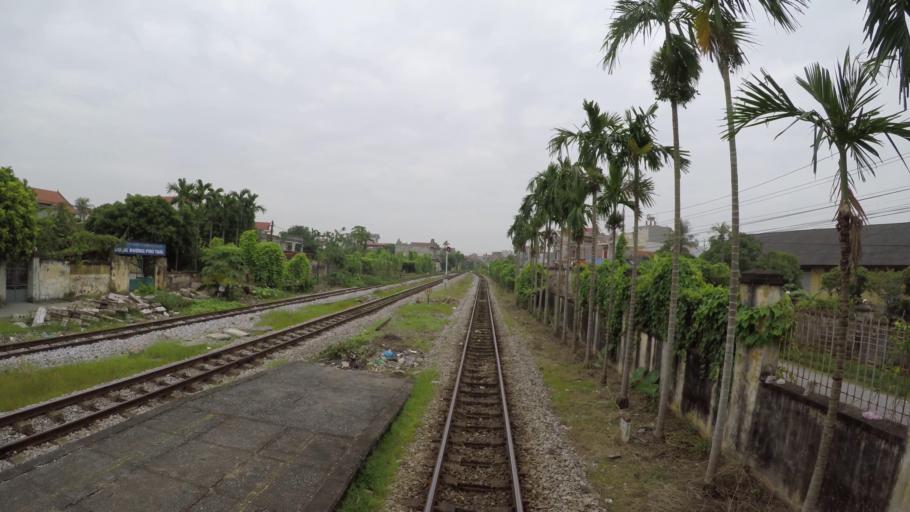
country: VN
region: Hai Duong
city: Phu Thai
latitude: 20.9701
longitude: 106.4971
